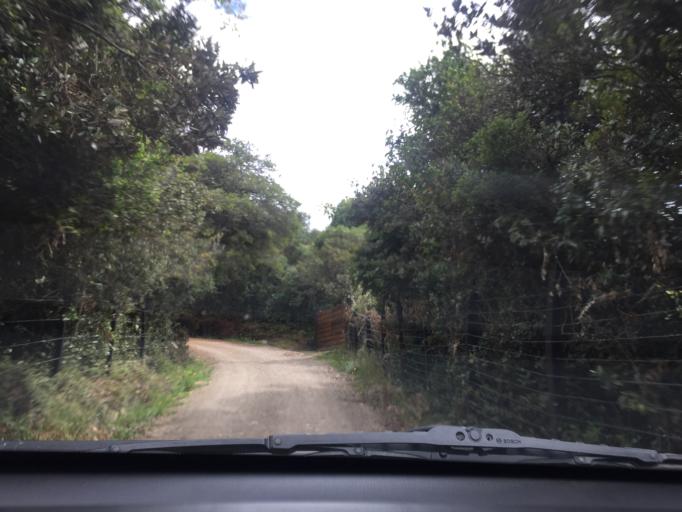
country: CO
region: Cundinamarca
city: Tocancipa
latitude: 4.9605
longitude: -73.8858
